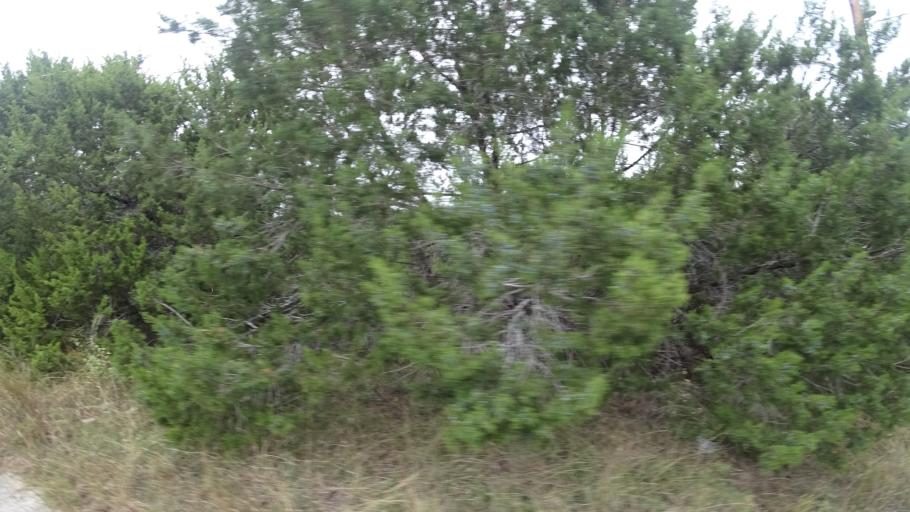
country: US
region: Texas
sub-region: Travis County
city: Hudson Bend
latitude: 30.3719
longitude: -97.9204
